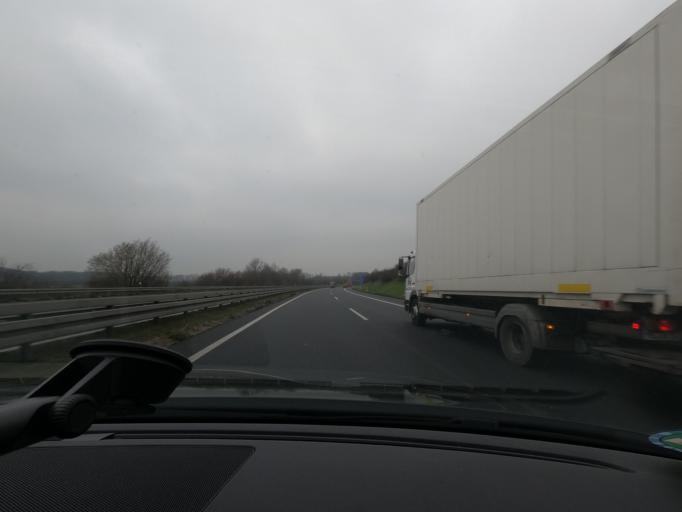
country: DE
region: North Rhine-Westphalia
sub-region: Regierungsbezirk Dusseldorf
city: Nettetal
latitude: 51.3072
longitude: 6.2301
